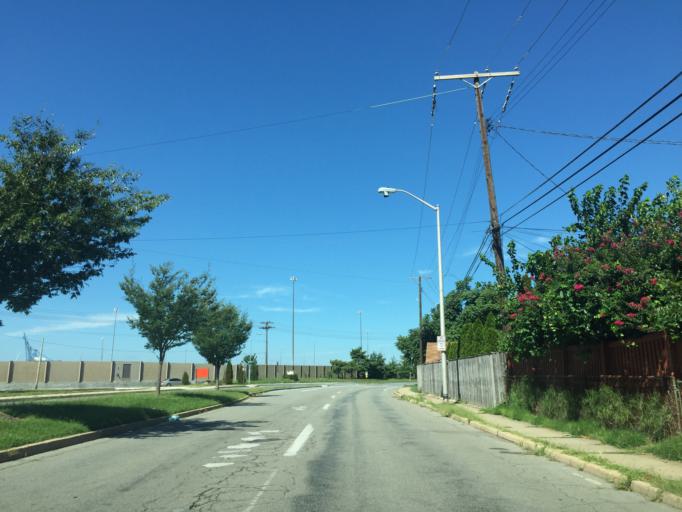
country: US
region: Maryland
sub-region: Baltimore County
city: Dundalk
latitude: 39.2458
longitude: -76.5138
